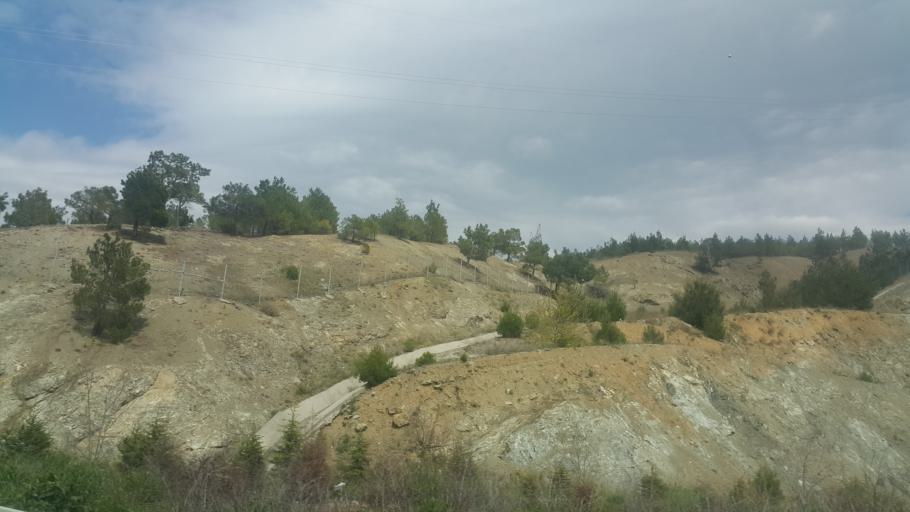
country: TR
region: Adana
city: Pozanti
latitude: 37.4494
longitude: 34.8818
